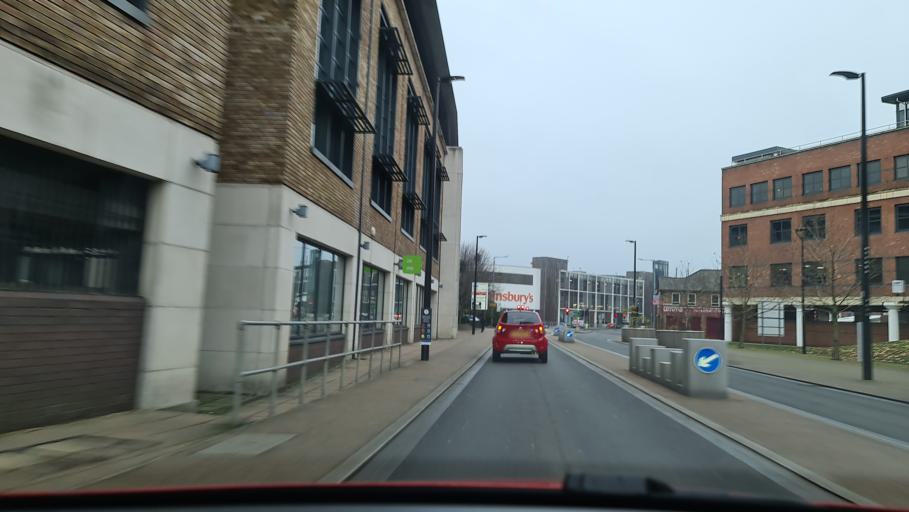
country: GB
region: England
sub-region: Buckinghamshire
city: High Wycombe
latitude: 51.6328
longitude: -0.7581
